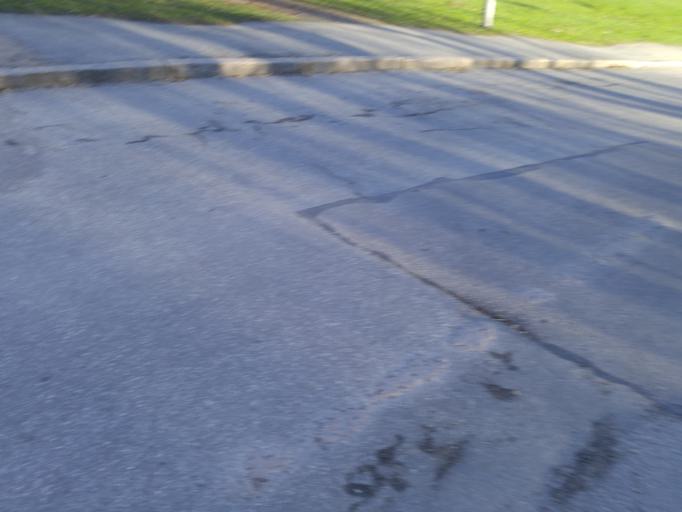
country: SE
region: Vaestra Goetaland
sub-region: Goteborg
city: Majorna
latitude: 57.6744
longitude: 11.9197
